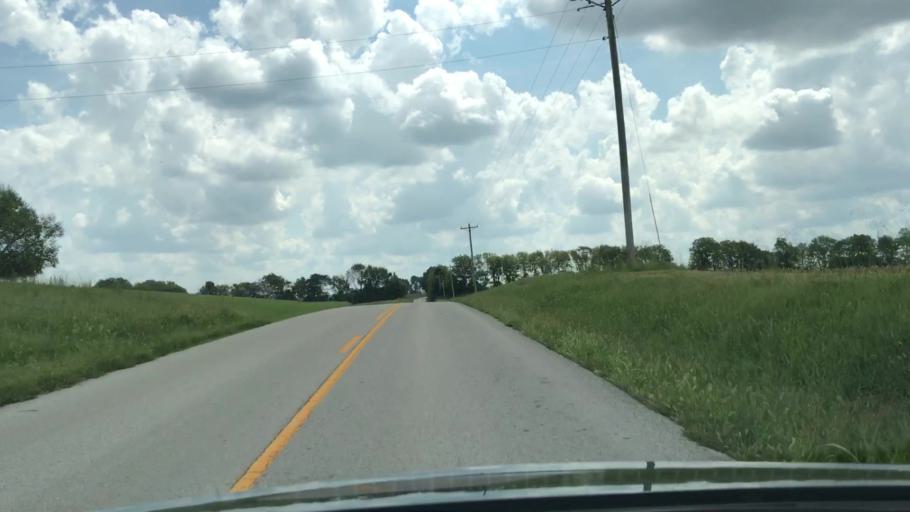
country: US
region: Kentucky
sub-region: Todd County
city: Elkton
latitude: 36.7851
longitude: -87.1286
